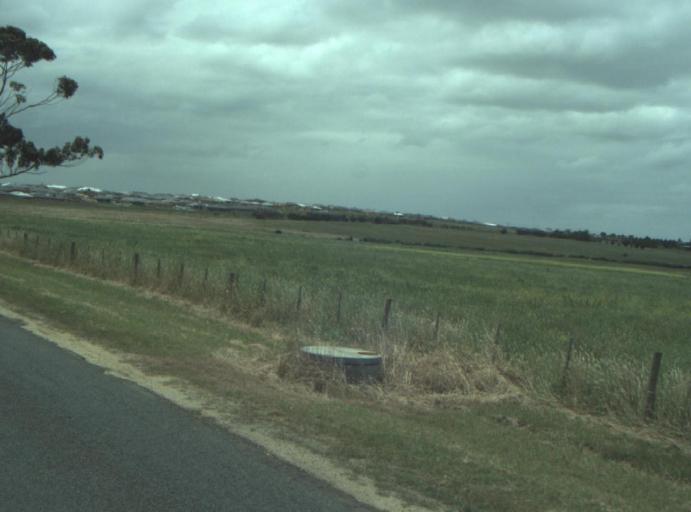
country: AU
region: Victoria
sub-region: Greater Geelong
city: Wandana Heights
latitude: -38.2213
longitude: 144.3000
